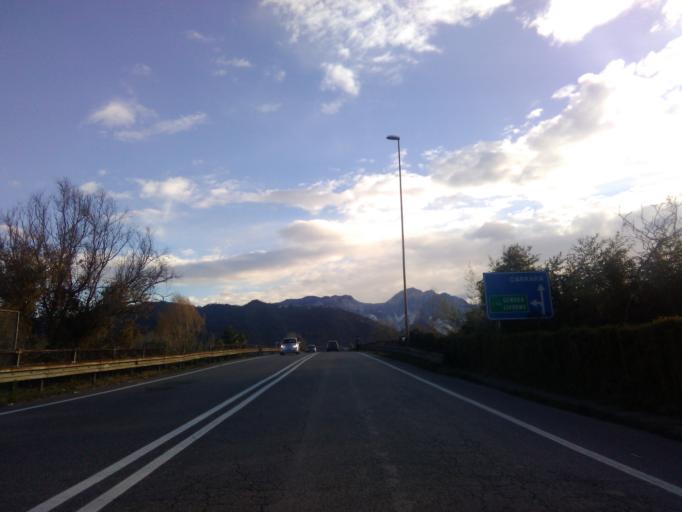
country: IT
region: Tuscany
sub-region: Provincia di Massa-Carrara
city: Marina di Carrara
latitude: 44.0499
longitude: 10.0362
